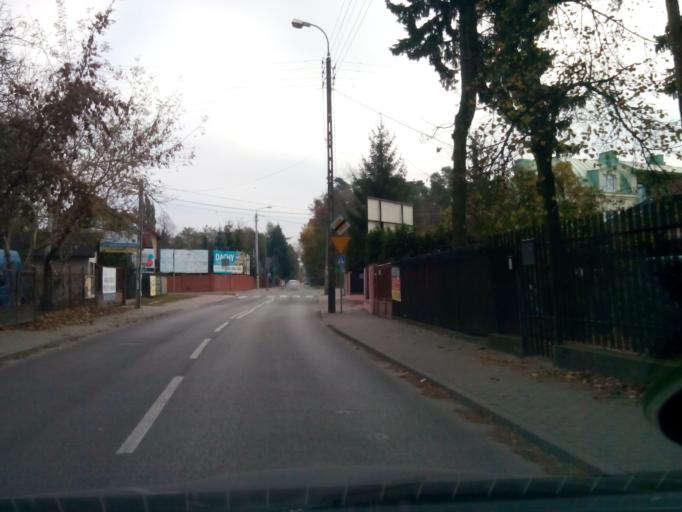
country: PL
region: Masovian Voivodeship
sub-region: Powiat pruszkowski
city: Komorow
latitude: 52.1491
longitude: 20.8033
